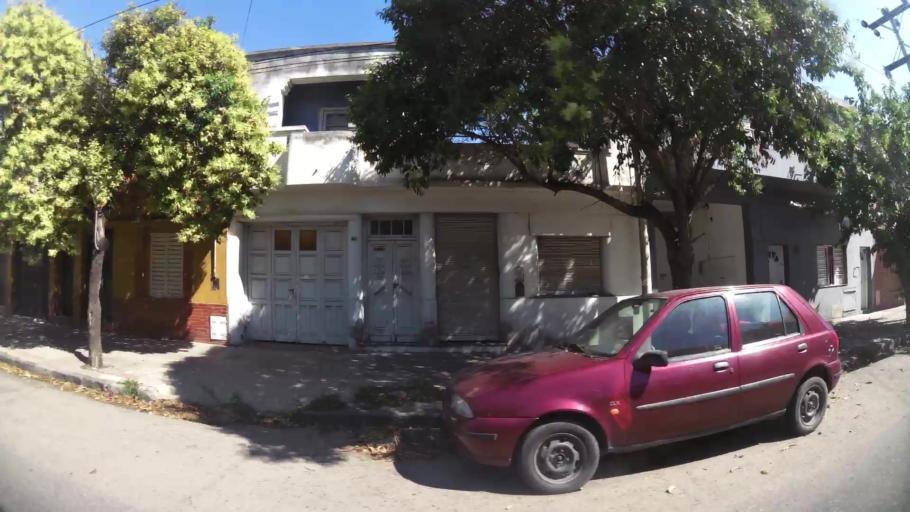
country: AR
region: Cordoba
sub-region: Departamento de Capital
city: Cordoba
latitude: -31.4020
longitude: -64.1735
